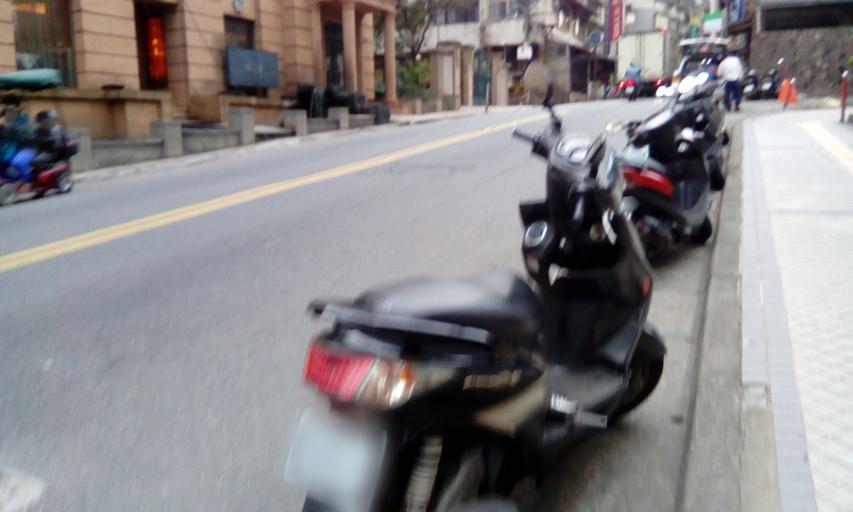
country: TW
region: Taipei
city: Taipei
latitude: 25.1758
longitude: 121.4390
